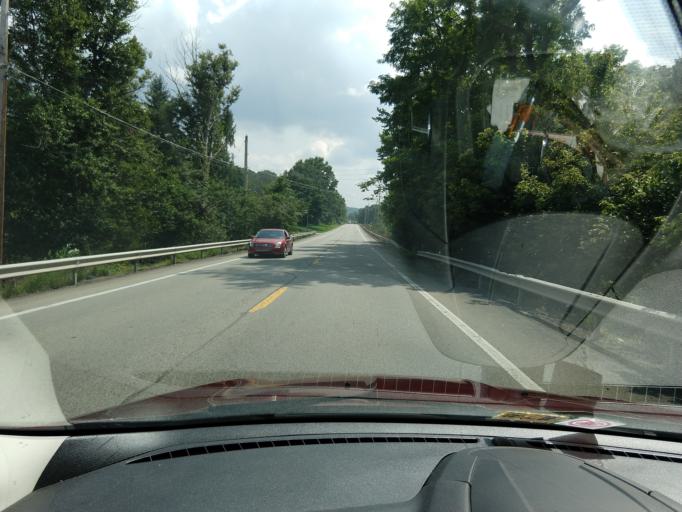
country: US
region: Pennsylvania
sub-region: Washington County
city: East Washington
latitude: 40.1616
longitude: -80.1326
